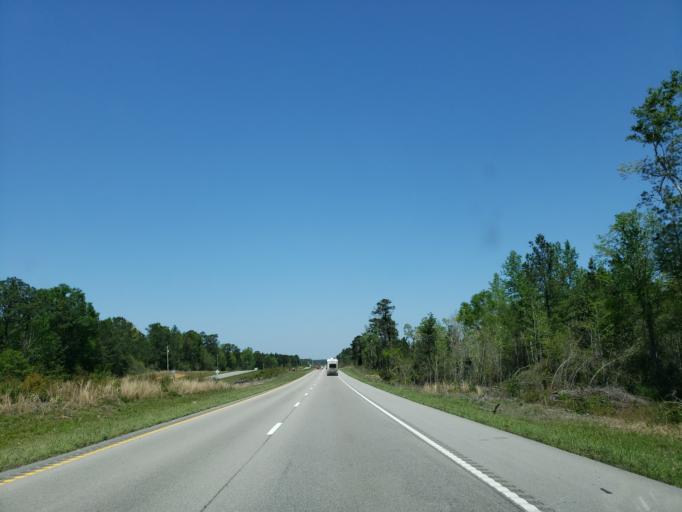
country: US
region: Mississippi
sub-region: Stone County
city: Wiggins
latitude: 30.9570
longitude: -89.1902
